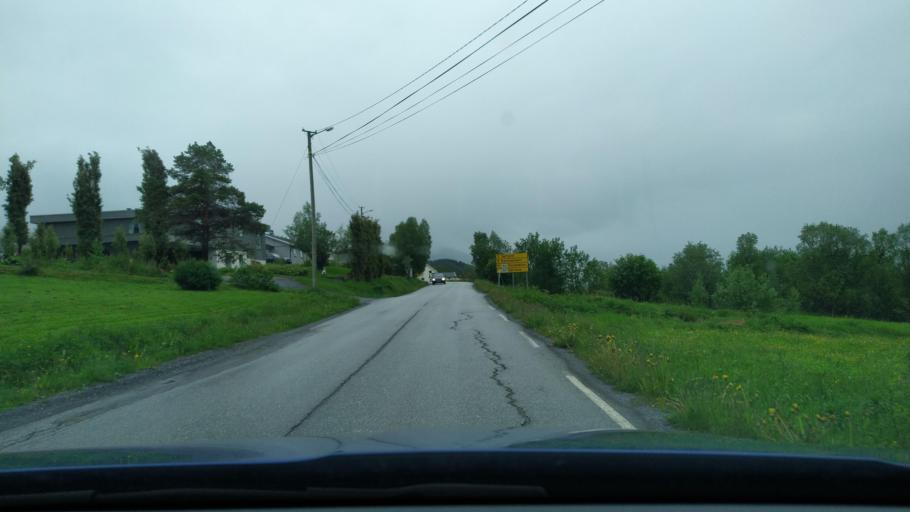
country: NO
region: Troms
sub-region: Dyroy
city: Brostadbotn
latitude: 69.0842
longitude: 17.6907
